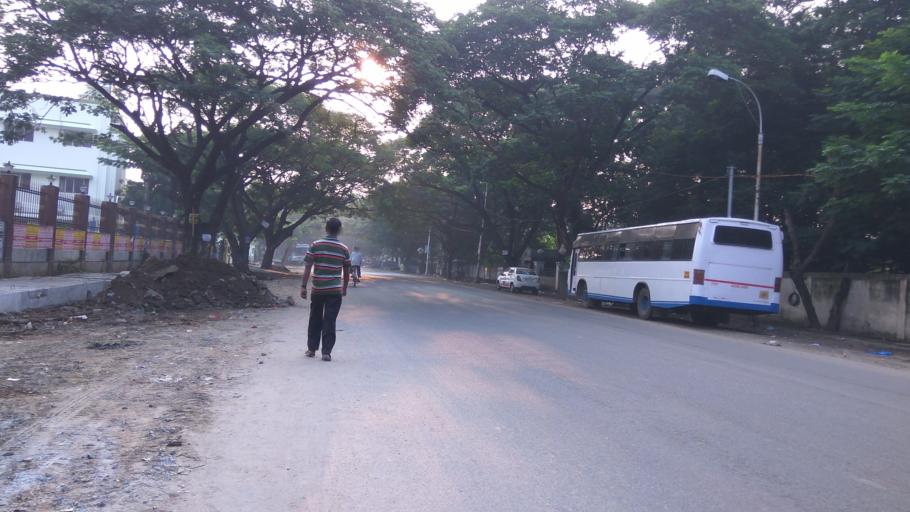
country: IN
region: Tamil Nadu
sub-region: Kancheepuram
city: Alandur
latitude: 13.0134
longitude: 80.2053
